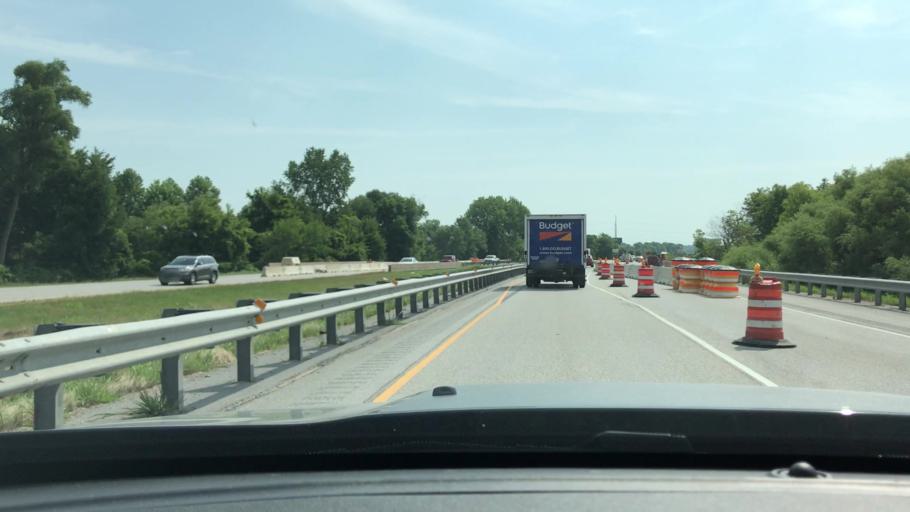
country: US
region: Illinois
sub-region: Rock Island County
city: Carbon Cliff
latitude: 41.4630
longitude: -90.3917
